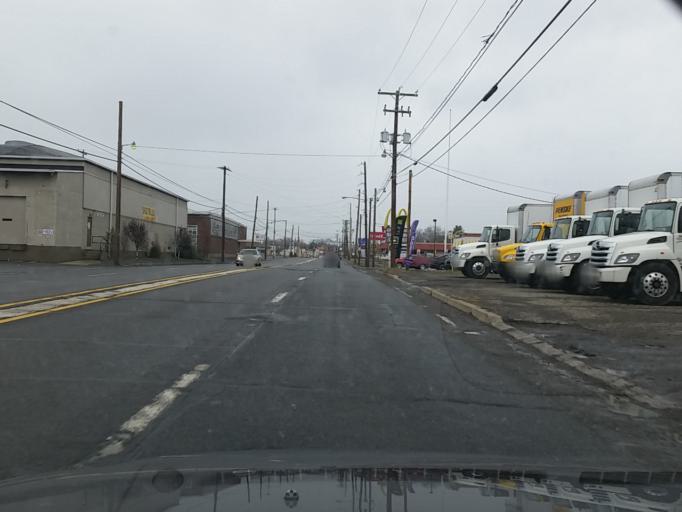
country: US
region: Pennsylvania
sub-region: Luzerne County
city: Larksville
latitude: 41.2313
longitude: -75.9230
